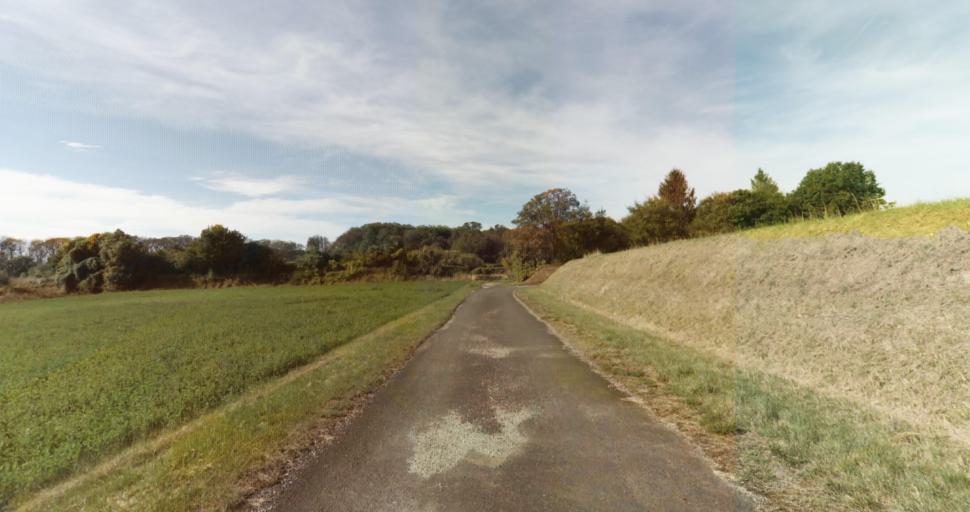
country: FR
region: Lower Normandy
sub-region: Departement de l'Orne
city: Sees
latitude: 48.7020
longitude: 0.2170
